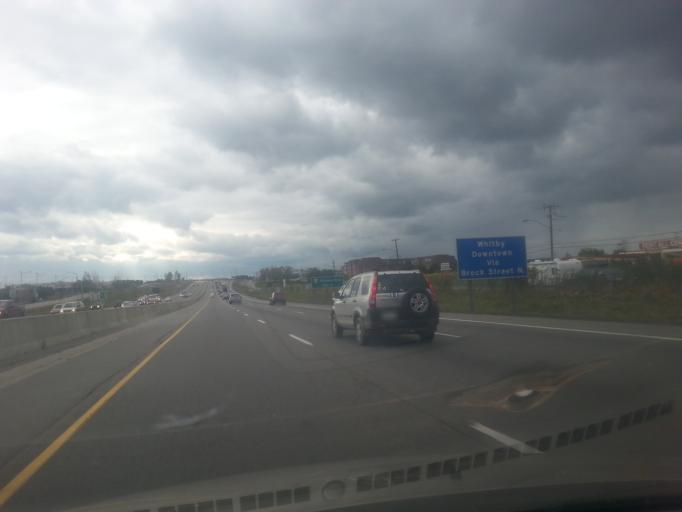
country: CA
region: Ontario
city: Oshawa
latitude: 43.8722
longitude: -78.8920
